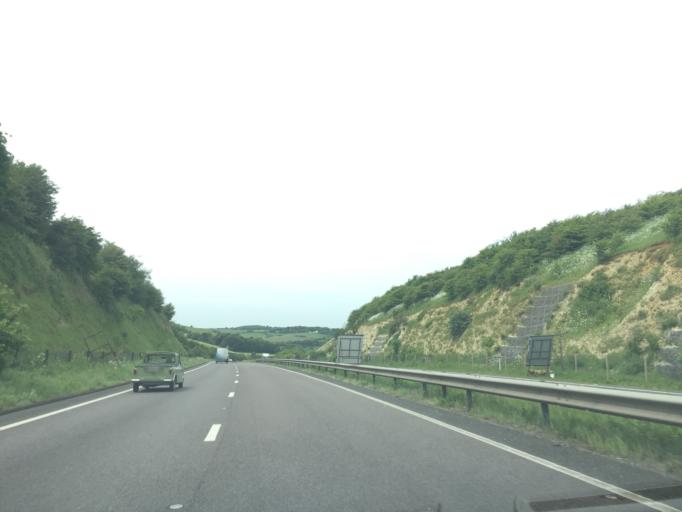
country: GB
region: England
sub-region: Kent
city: Folkestone
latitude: 51.1128
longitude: 1.2058
